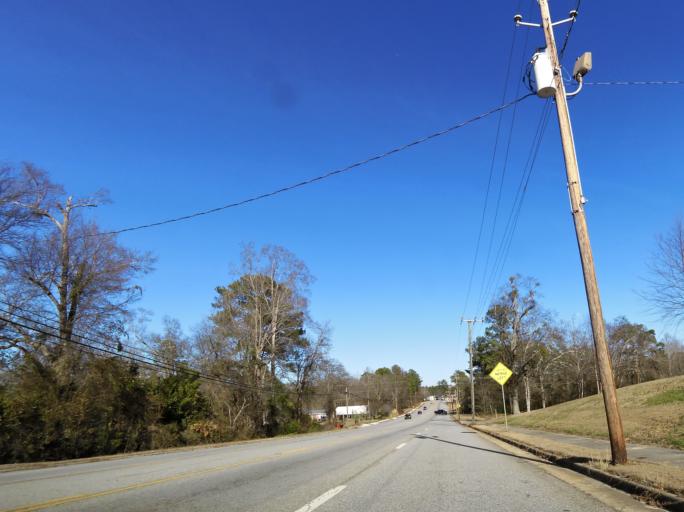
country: US
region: Georgia
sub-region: Crawford County
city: Roberta
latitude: 32.7232
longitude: -84.0105
